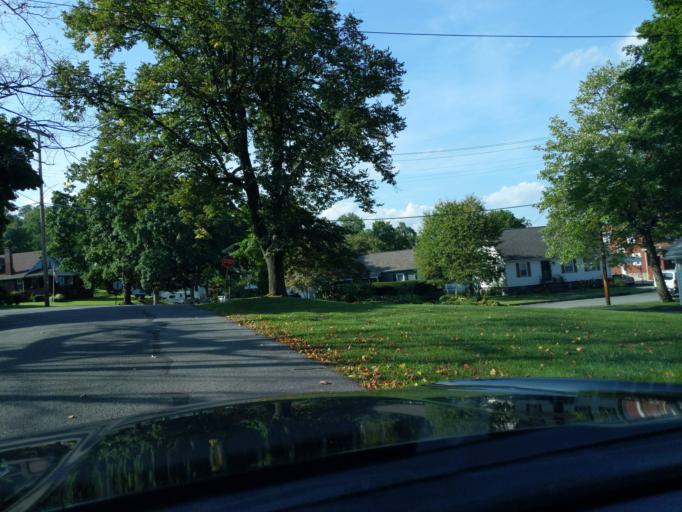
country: US
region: Pennsylvania
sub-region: Blair County
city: Lakemont
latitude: 40.4799
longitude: -78.4080
